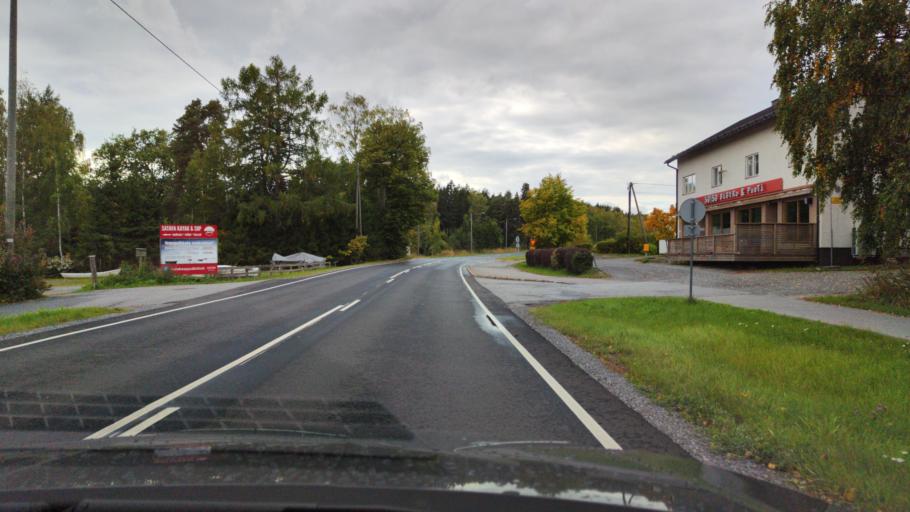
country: FI
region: Varsinais-Suomi
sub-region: Turku
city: Turku
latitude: 60.3766
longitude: 22.2166
